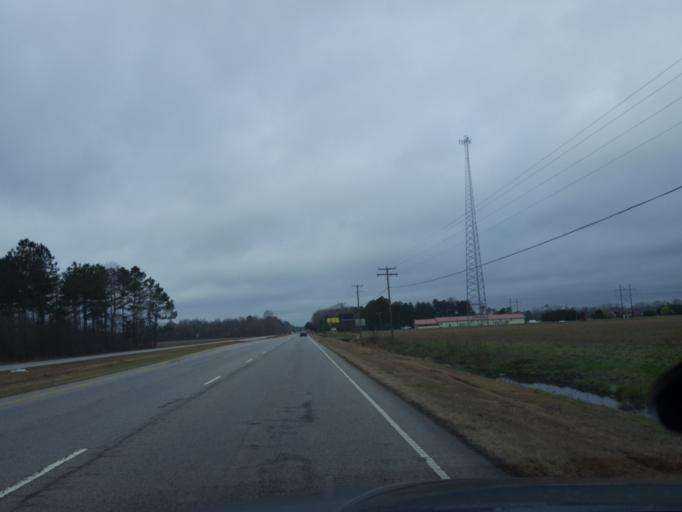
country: US
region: North Carolina
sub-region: Washington County
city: Plymouth
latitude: 35.8115
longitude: -76.8581
